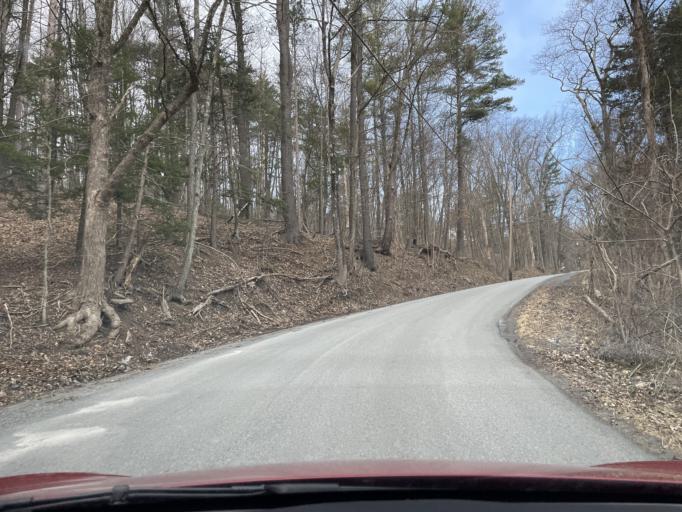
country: US
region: New York
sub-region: Ulster County
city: Saugerties
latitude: 42.1045
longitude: -73.9819
